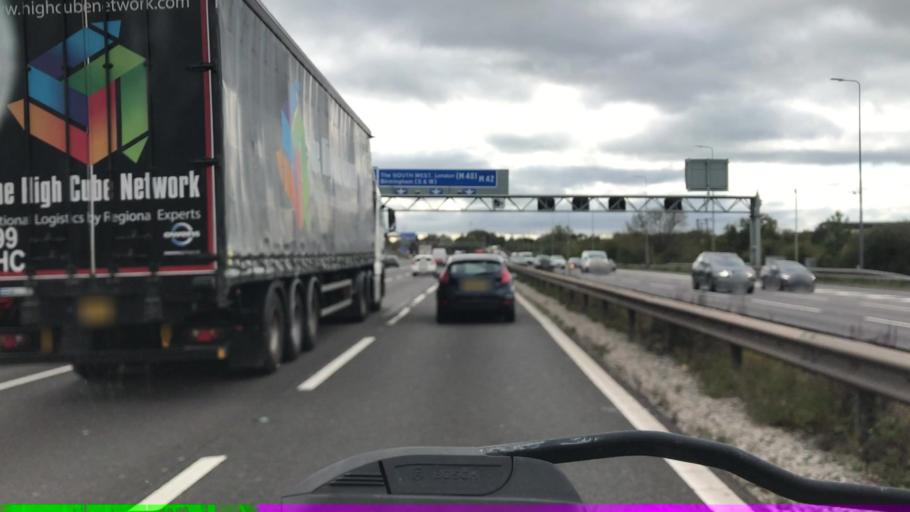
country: GB
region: England
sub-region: Solihull
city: Solihull
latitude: 52.3846
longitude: -1.7820
